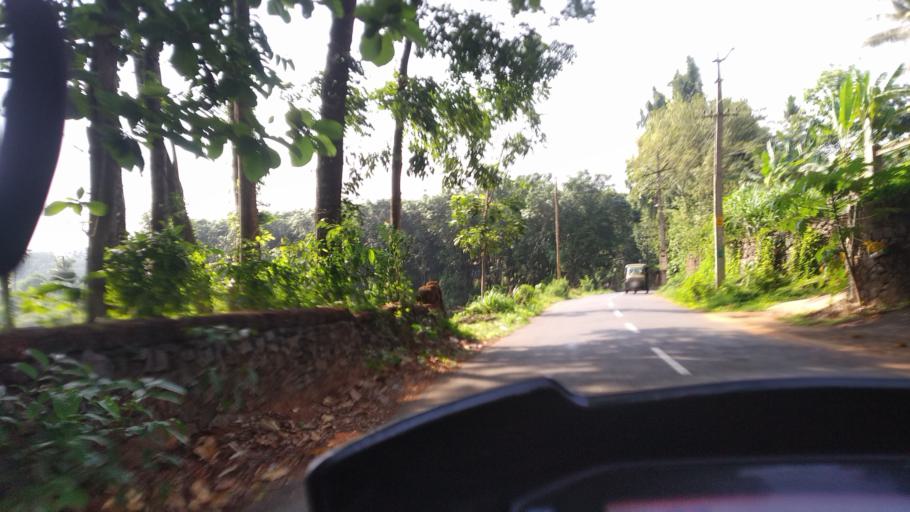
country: IN
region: Kerala
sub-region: Kottayam
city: Palackattumala
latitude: 9.8002
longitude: 76.5843
